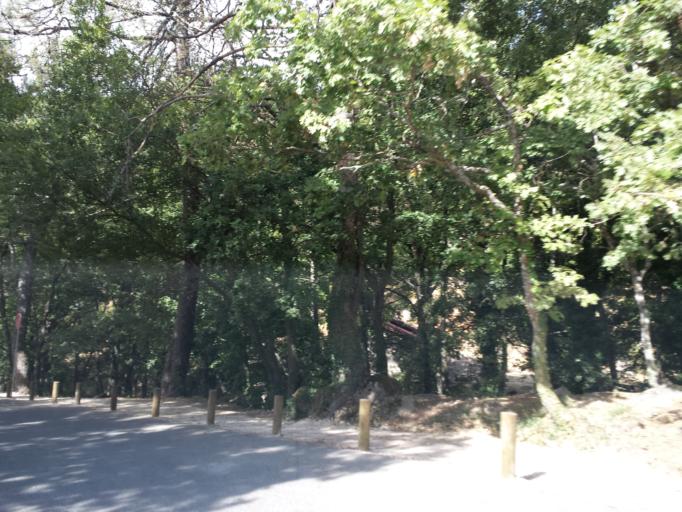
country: ES
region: Castille and Leon
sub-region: Provincia de Avila
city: Piedralaves
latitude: 40.3251
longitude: -4.7024
